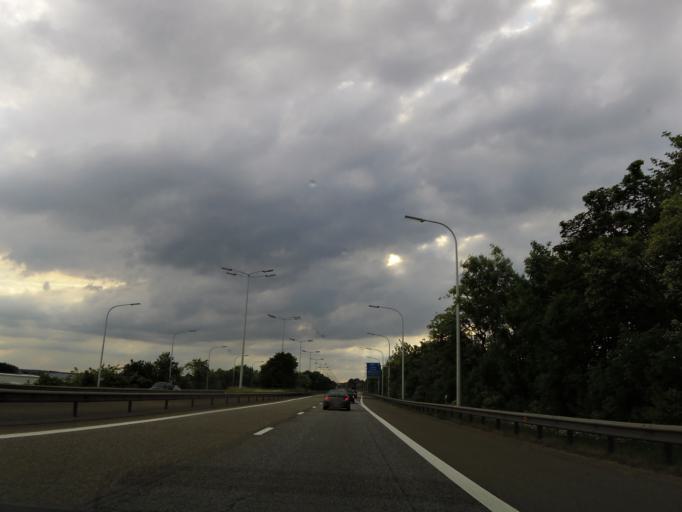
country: BE
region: Flanders
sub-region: Provincie Limburg
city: Maasmechelen
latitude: 50.9527
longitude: 5.7037
